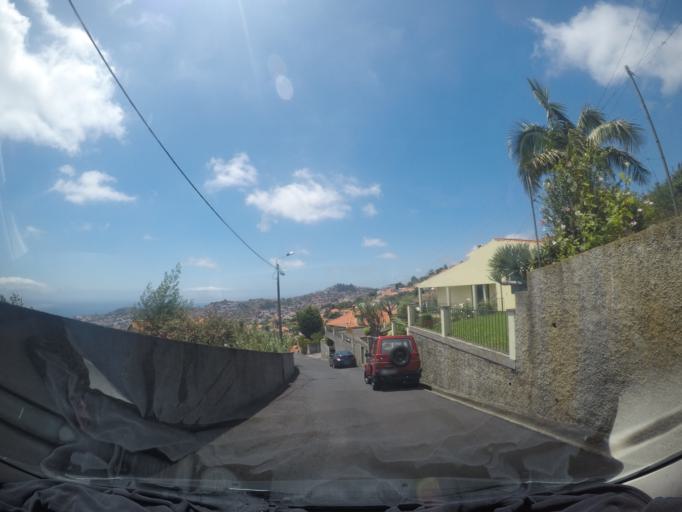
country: PT
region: Madeira
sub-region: Funchal
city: Nossa Senhora do Monte
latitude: 32.6745
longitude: -16.9254
